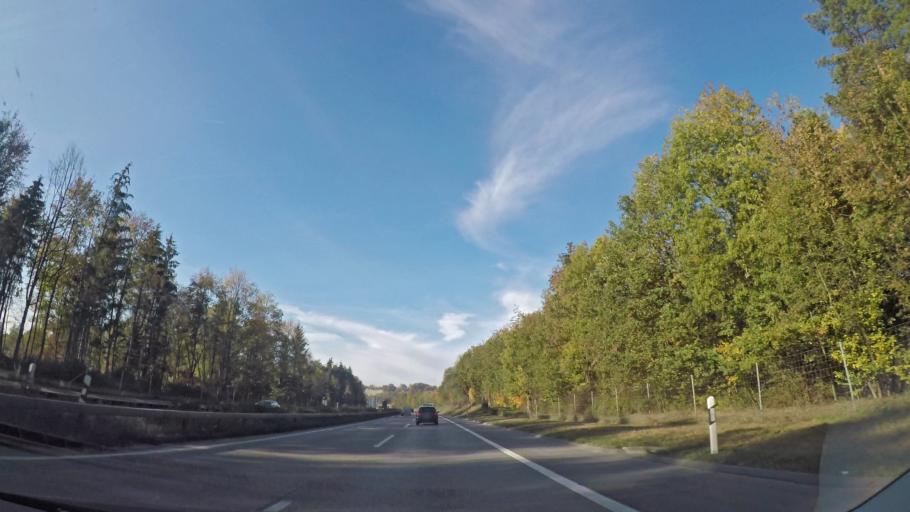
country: CH
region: Bern
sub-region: Thun District
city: Heimberg
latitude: 46.7865
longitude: 7.6004
